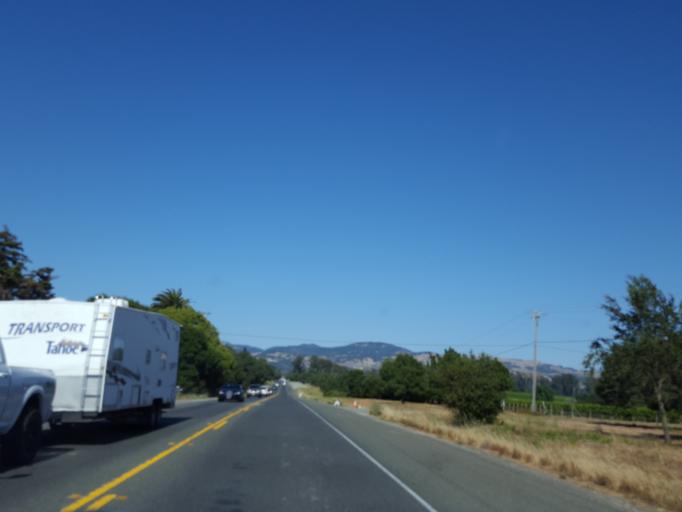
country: US
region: California
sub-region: Napa County
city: Napa
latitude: 38.2566
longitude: -122.3244
